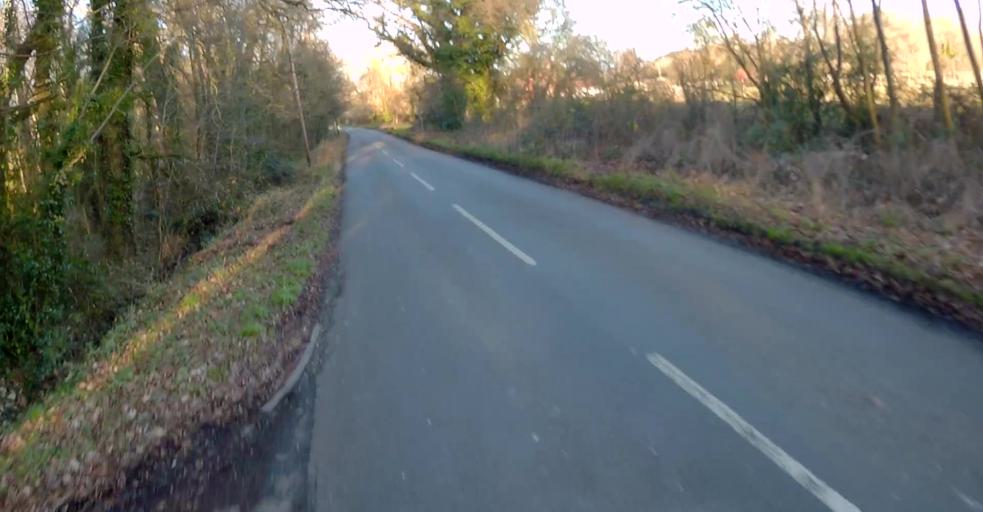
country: GB
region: England
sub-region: Hampshire
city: Hook
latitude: 51.2885
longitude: -0.9806
